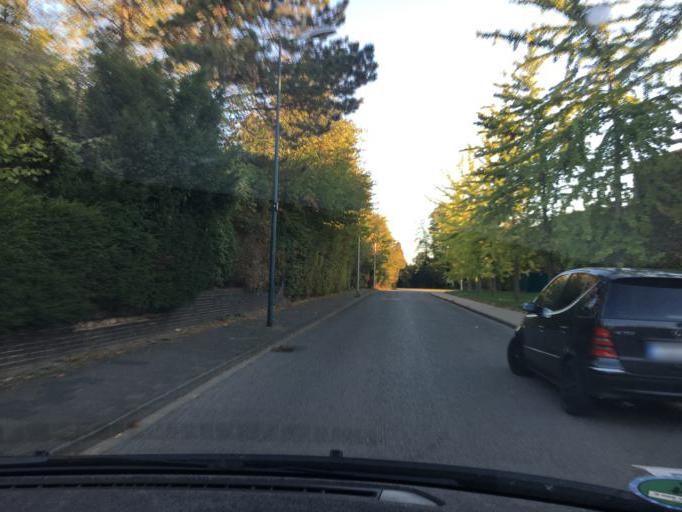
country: DE
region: North Rhine-Westphalia
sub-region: Regierungsbezirk Koln
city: Dueren
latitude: 50.8137
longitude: 6.4450
